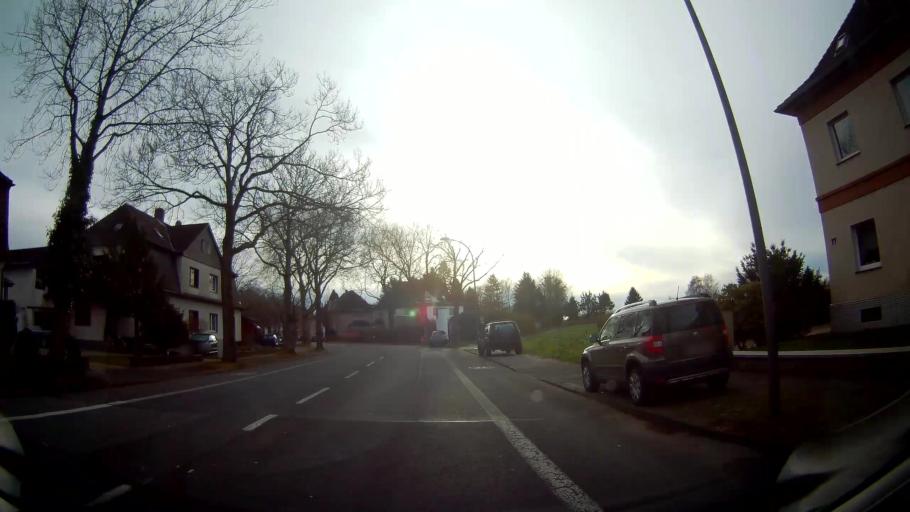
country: DE
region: North Rhine-Westphalia
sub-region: Regierungsbezirk Arnsberg
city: Herne
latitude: 51.5200
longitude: 7.2503
